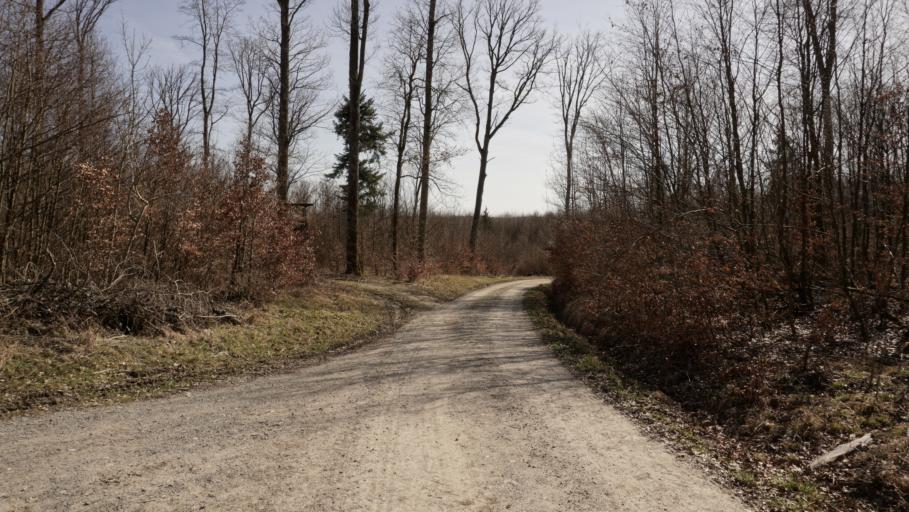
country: DE
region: Baden-Wuerttemberg
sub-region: Karlsruhe Region
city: Mosbach
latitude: 49.3815
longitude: 9.1431
